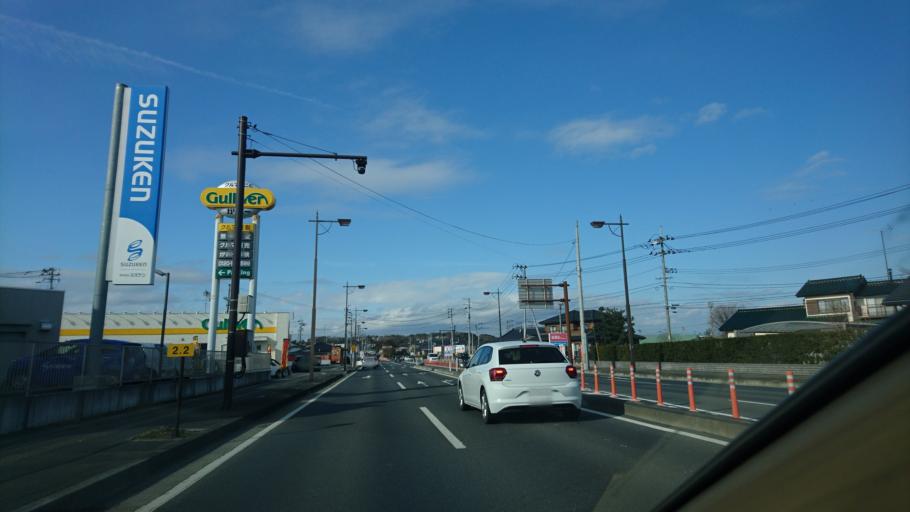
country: JP
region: Miyagi
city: Ishinomaki
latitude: 38.4512
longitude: 141.2662
